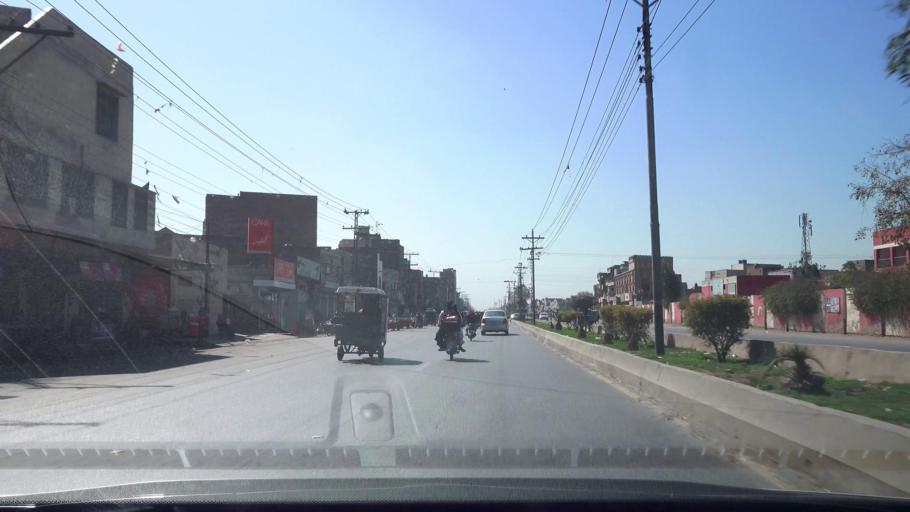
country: PK
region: Punjab
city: Faisalabad
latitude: 31.4113
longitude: 73.0625
